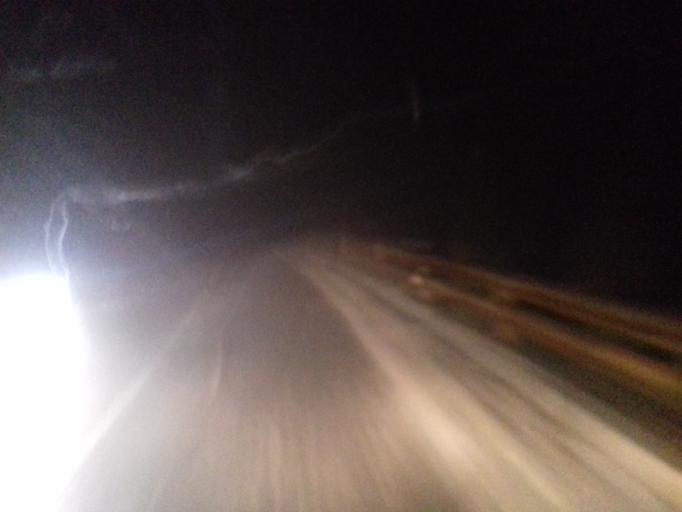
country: BA
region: Federation of Bosnia and Herzegovina
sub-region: Kanton Sarajevo
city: Sarajevo
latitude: 43.7706
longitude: 18.3605
